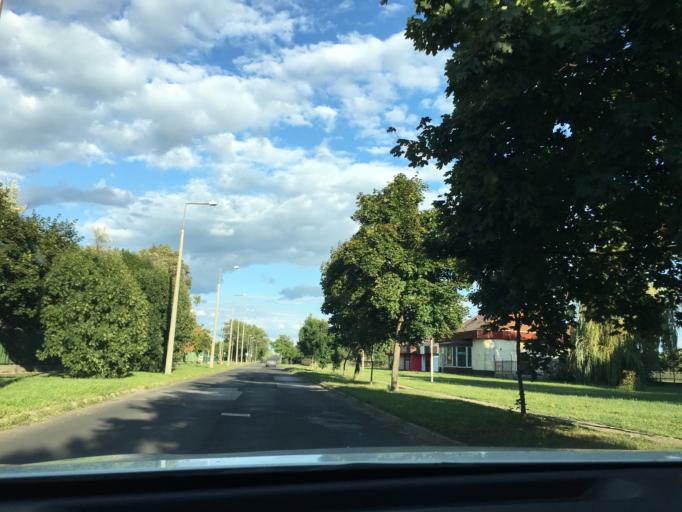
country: HU
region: Budapest
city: Budapest XVII. keruelet
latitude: 47.4793
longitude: 19.2346
